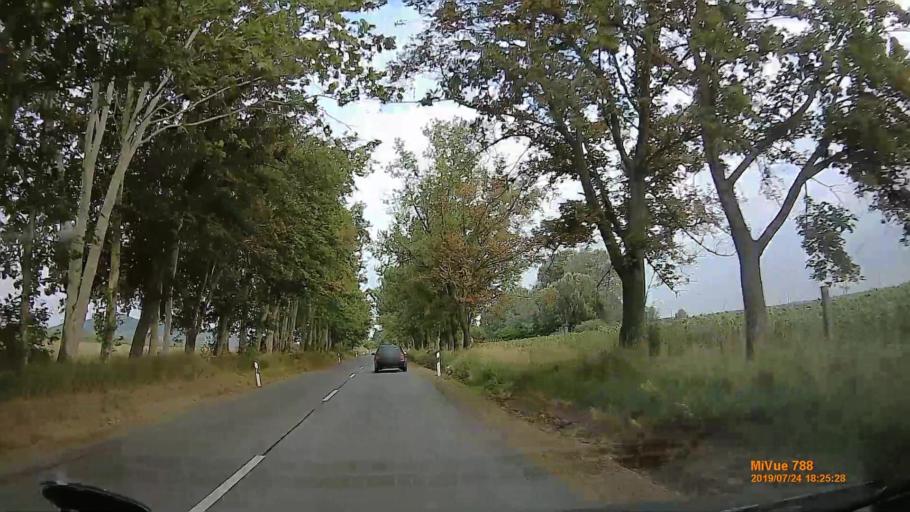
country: HU
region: Borsod-Abauj-Zemplen
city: Tarcal
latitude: 48.1504
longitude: 21.3170
